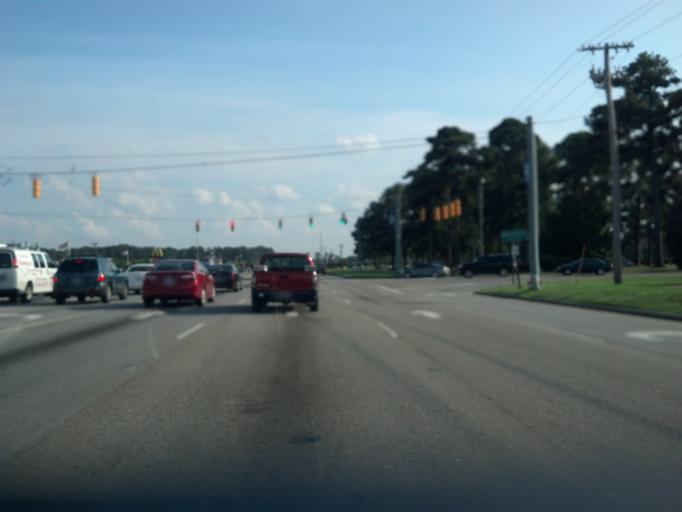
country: US
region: North Carolina
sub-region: Pitt County
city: Summerfield
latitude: 35.5526
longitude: -77.4060
